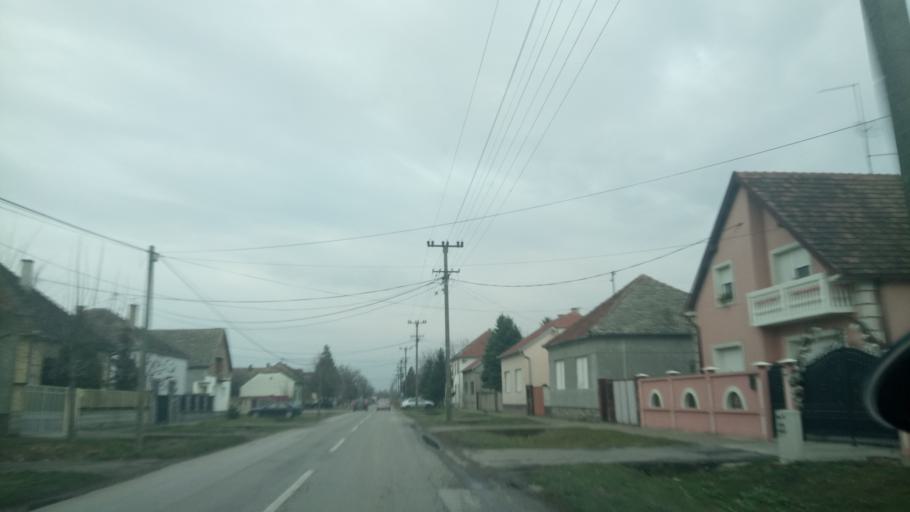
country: RS
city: Vojka
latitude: 44.9402
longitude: 20.1527
